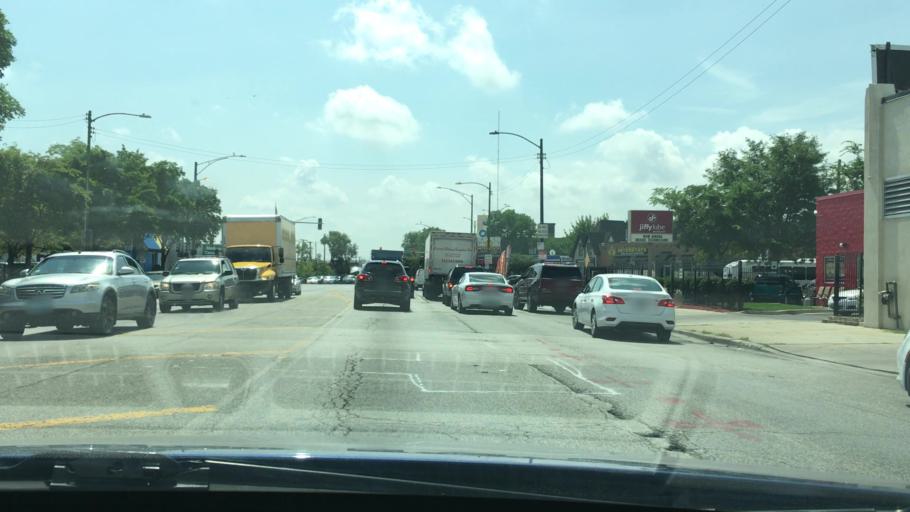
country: US
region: Illinois
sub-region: Cook County
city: Chicago
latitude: 41.8659
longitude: -87.6861
